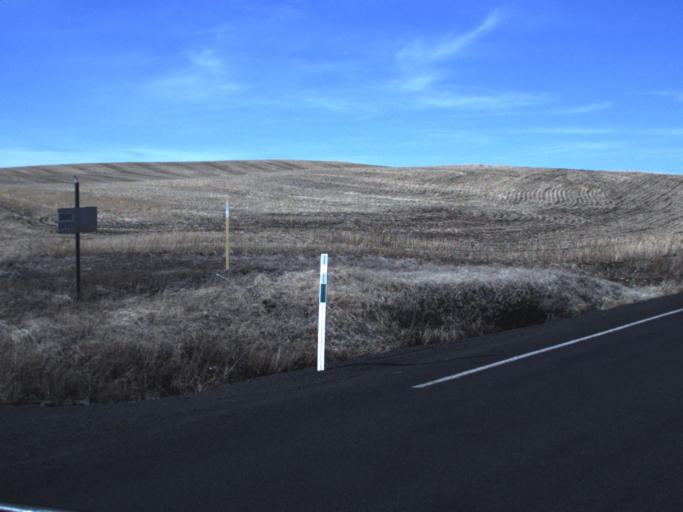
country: US
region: Washington
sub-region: Lincoln County
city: Davenport
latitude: 47.7233
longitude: -118.1528
